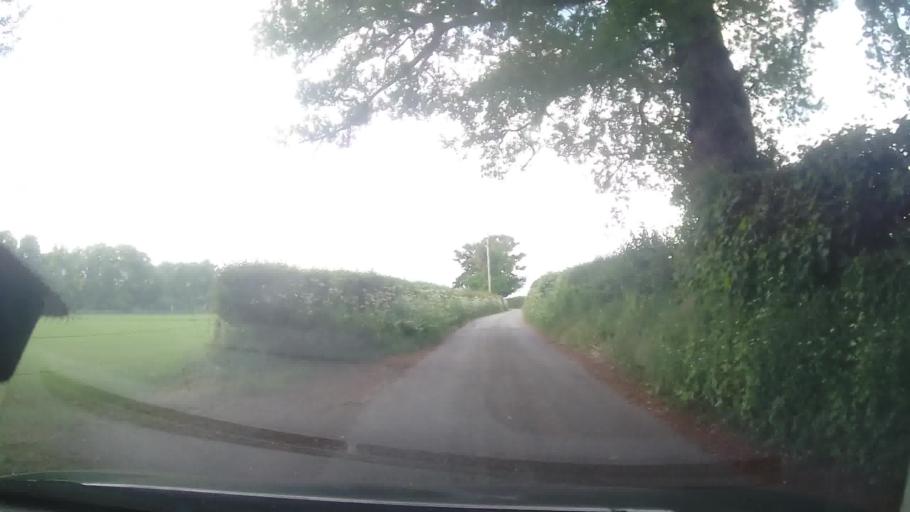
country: GB
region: England
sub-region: Shropshire
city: Clive
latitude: 52.8074
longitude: -2.7282
